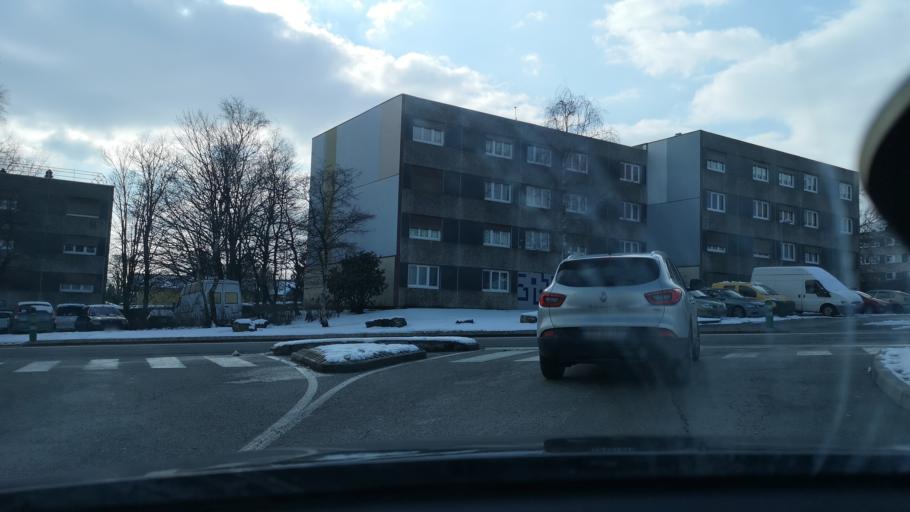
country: FR
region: Rhone-Alpes
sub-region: Departement de l'Ain
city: Bellegarde-sur-Valserine
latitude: 46.1227
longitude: 5.8133
